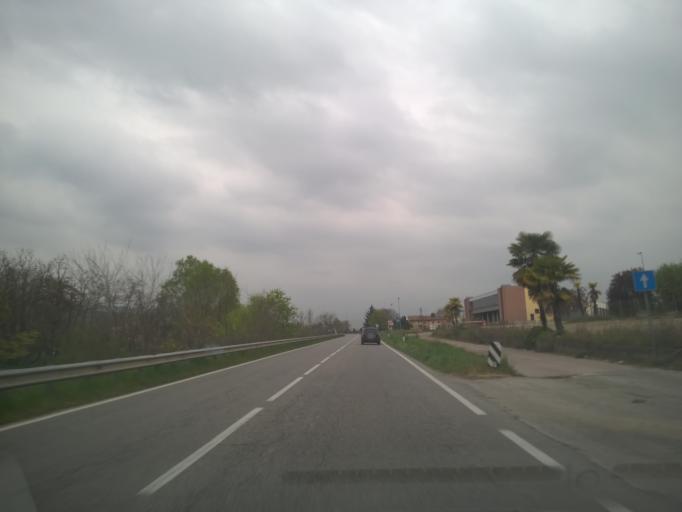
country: IT
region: Veneto
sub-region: Provincia di Vicenza
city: Castelnovo
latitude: 45.6183
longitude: 11.4627
